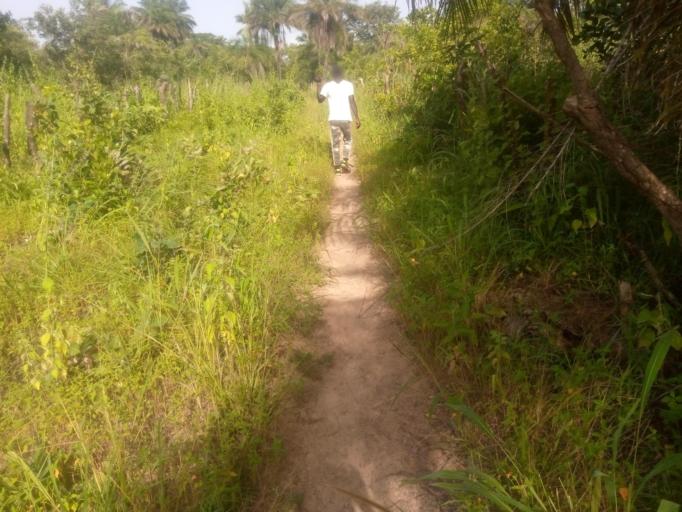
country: GM
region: Western
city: Gunjur
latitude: 13.0289
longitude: -16.7285
